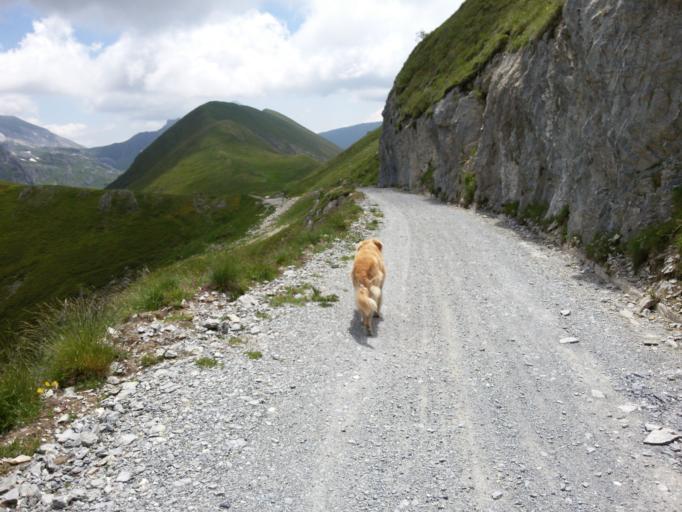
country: IT
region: Piedmont
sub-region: Provincia di Cuneo
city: Limone Piemonte
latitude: 44.1648
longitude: 7.6264
